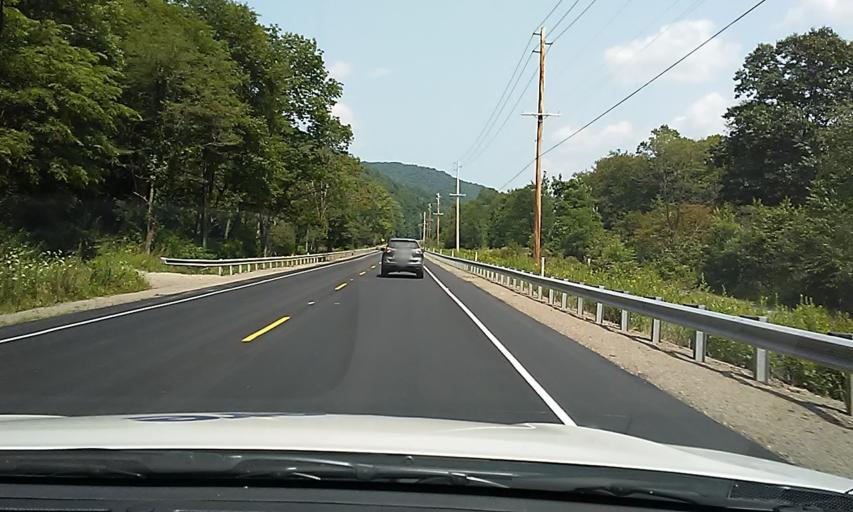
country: US
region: Pennsylvania
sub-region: Cameron County
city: Emporium
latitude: 41.4860
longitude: -78.3086
